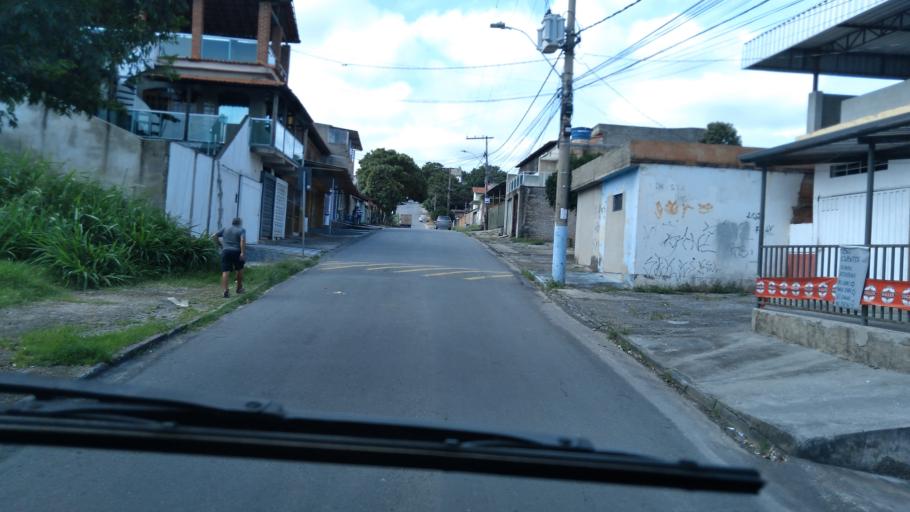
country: BR
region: Minas Gerais
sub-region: Santa Luzia
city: Santa Luzia
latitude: -19.8313
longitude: -43.8966
